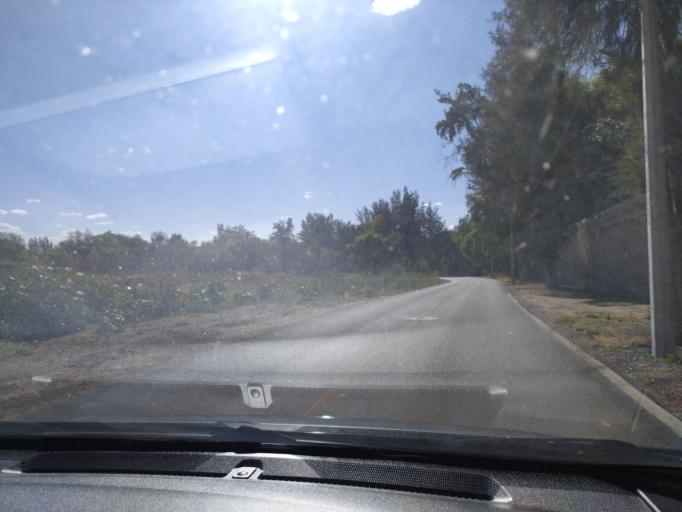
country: LA
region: Oudomxai
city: Muang La
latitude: 21.0438
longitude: 101.8357
